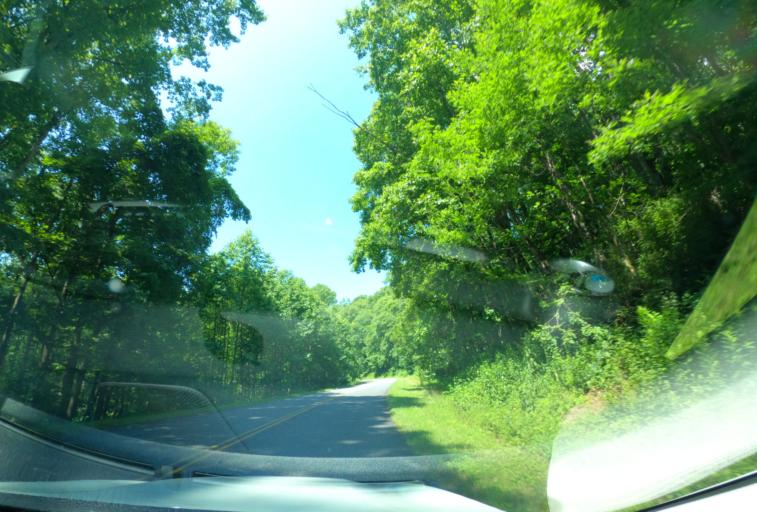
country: US
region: North Carolina
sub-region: Haywood County
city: Maggie Valley
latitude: 35.4433
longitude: -83.0836
